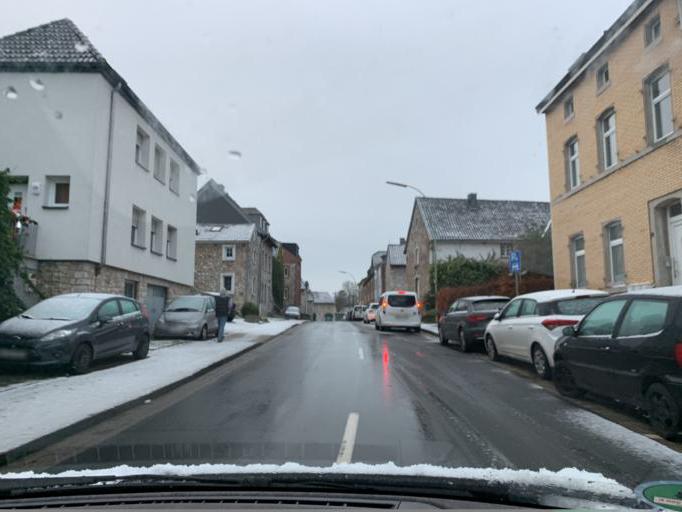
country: DE
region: North Rhine-Westphalia
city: Stolberg
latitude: 50.7331
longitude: 6.2248
